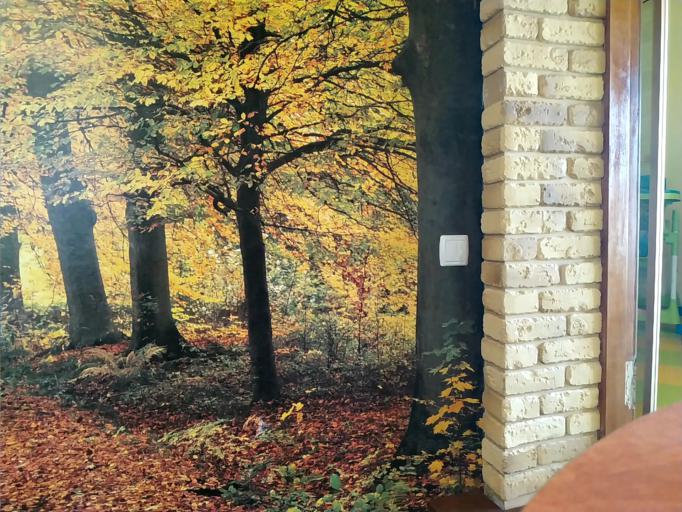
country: RU
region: Tverskaya
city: Rameshki
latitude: 57.5199
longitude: 35.9708
